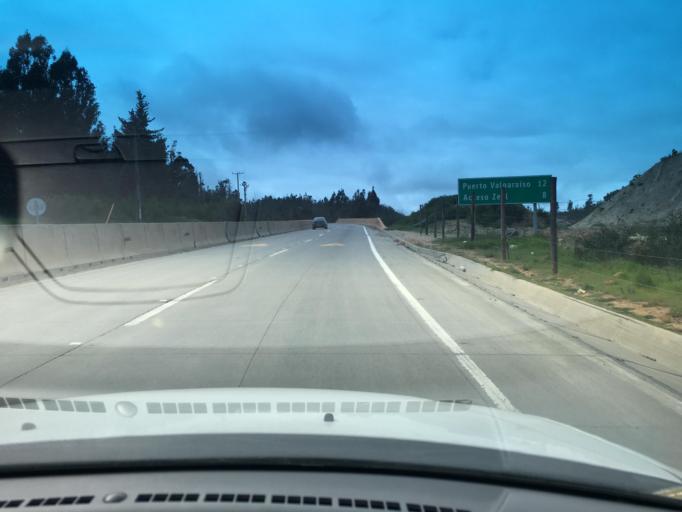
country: CL
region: Valparaiso
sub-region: Provincia de Valparaiso
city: Vina del Mar
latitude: -33.1045
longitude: -71.5729
